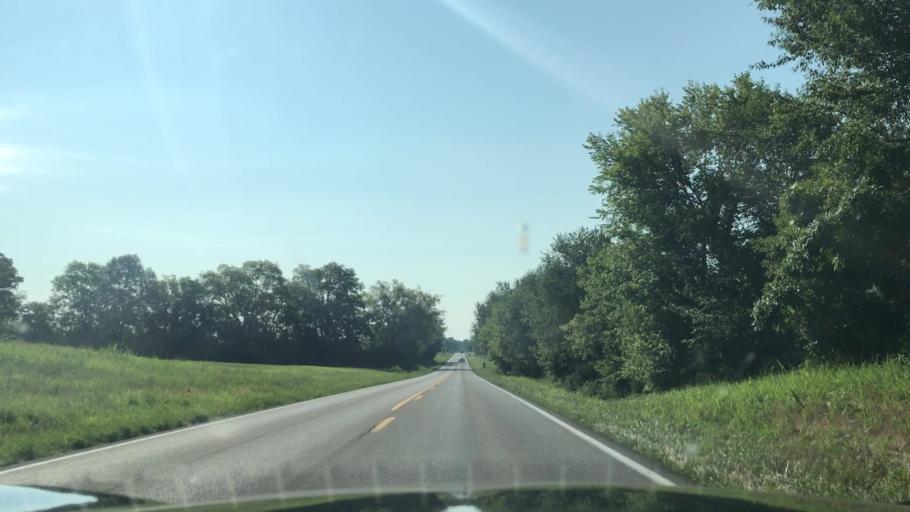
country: US
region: Kentucky
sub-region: Hart County
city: Horse Cave
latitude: 37.1717
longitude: -85.8572
